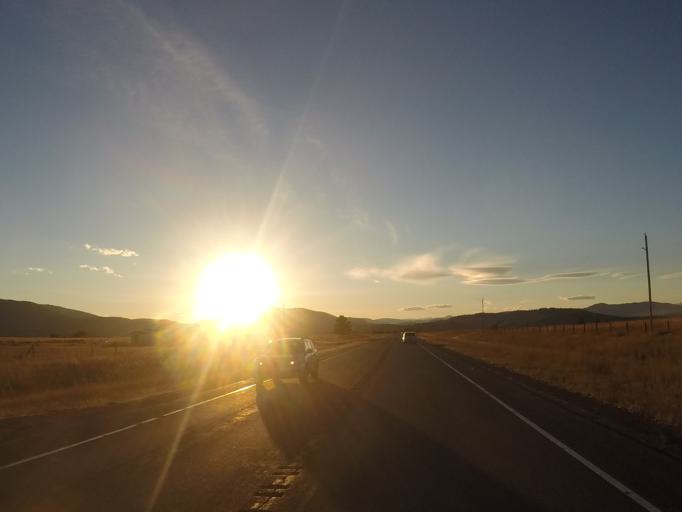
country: US
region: Montana
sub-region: Missoula County
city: Seeley Lake
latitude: 47.0201
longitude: -113.1107
